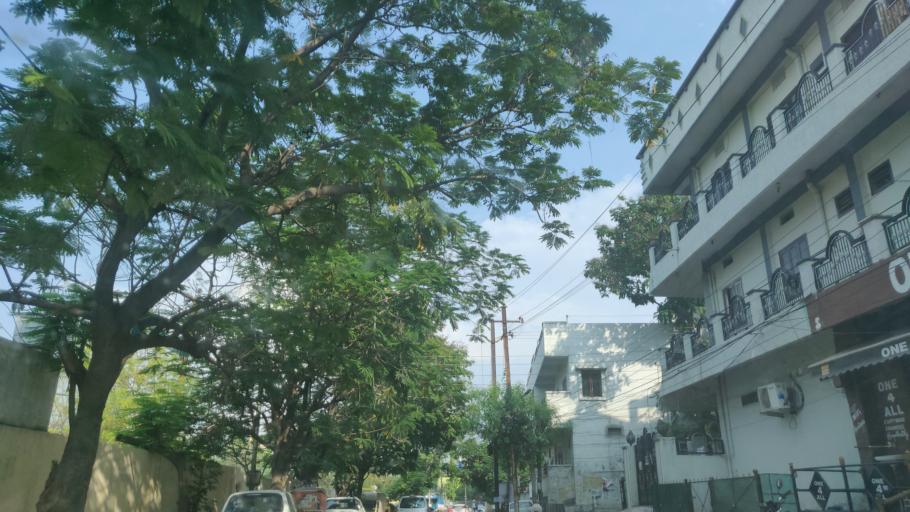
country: IN
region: Telangana
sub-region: Rangareddi
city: Gaddi Annaram
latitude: 17.3763
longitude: 78.5155
